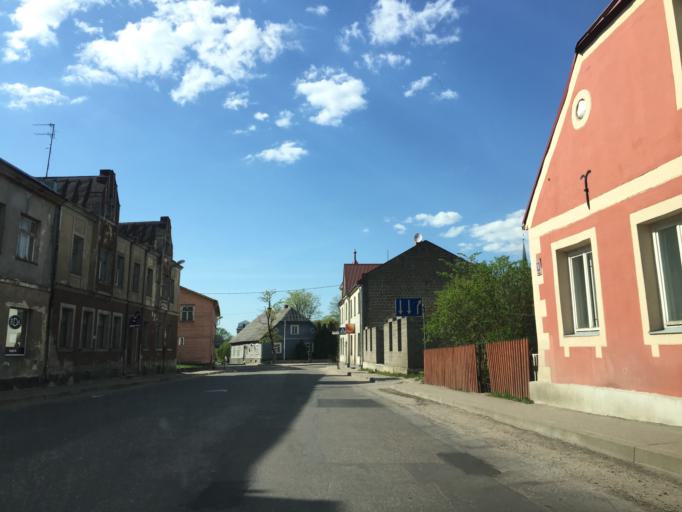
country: LV
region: Limbazu Rajons
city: Limbazi
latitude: 57.5136
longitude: 24.7168
